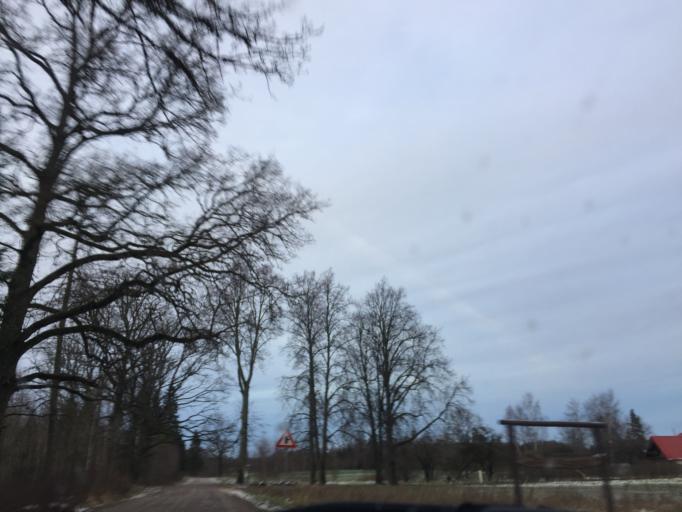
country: LV
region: Limbazu Rajons
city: Limbazi
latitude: 57.5594
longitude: 24.8168
